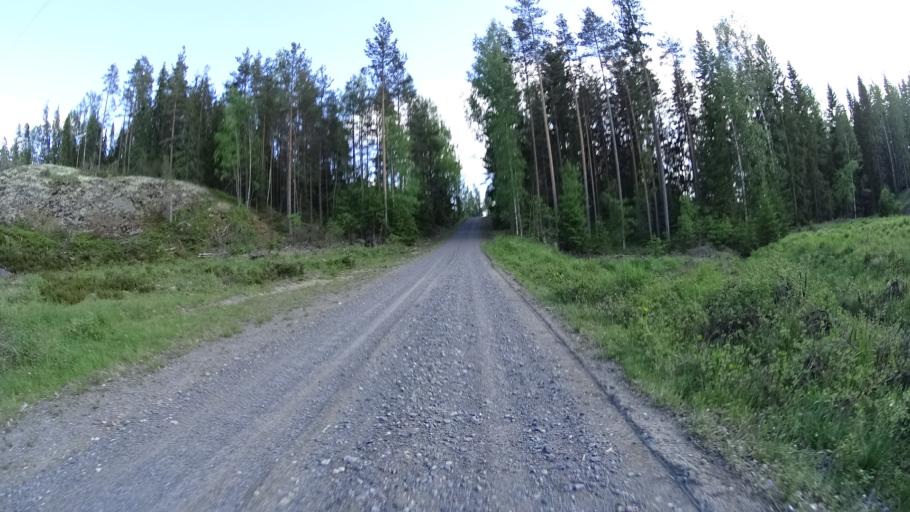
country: FI
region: Varsinais-Suomi
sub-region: Salo
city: Kisko
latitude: 60.1634
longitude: 23.4900
